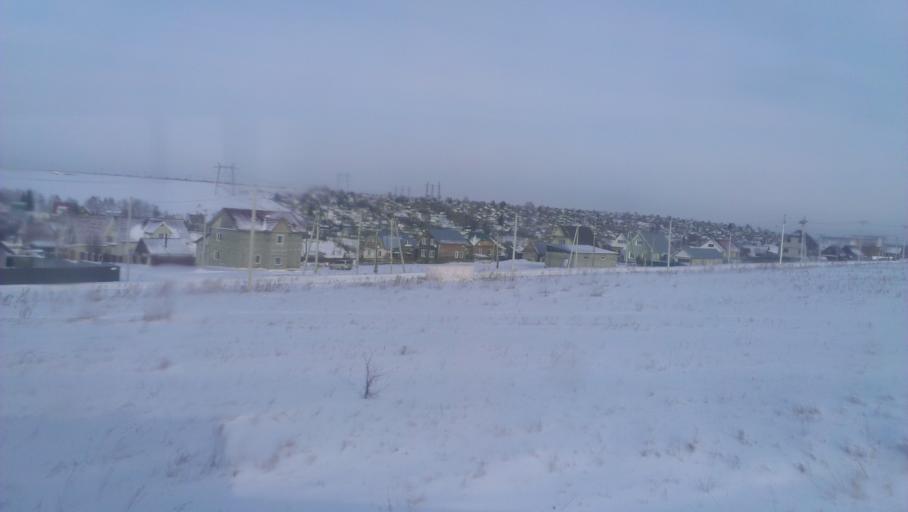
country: RU
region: Altai Krai
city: Gon'ba
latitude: 53.4133
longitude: 83.5542
